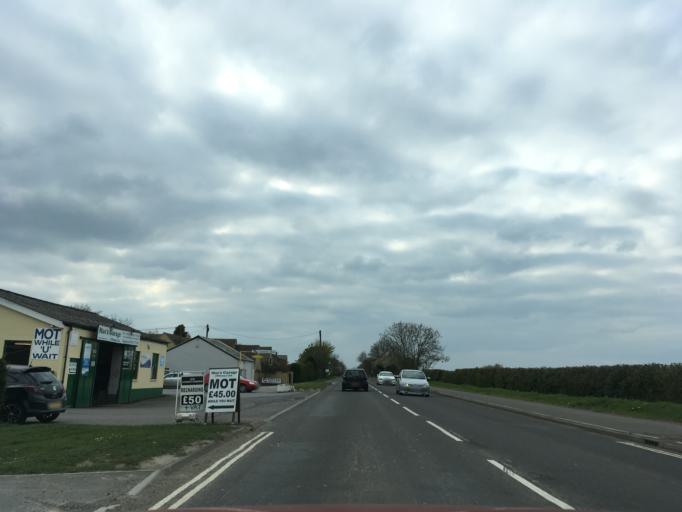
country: GB
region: England
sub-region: Oxfordshire
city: Witney
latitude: 51.7939
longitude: -1.5238
